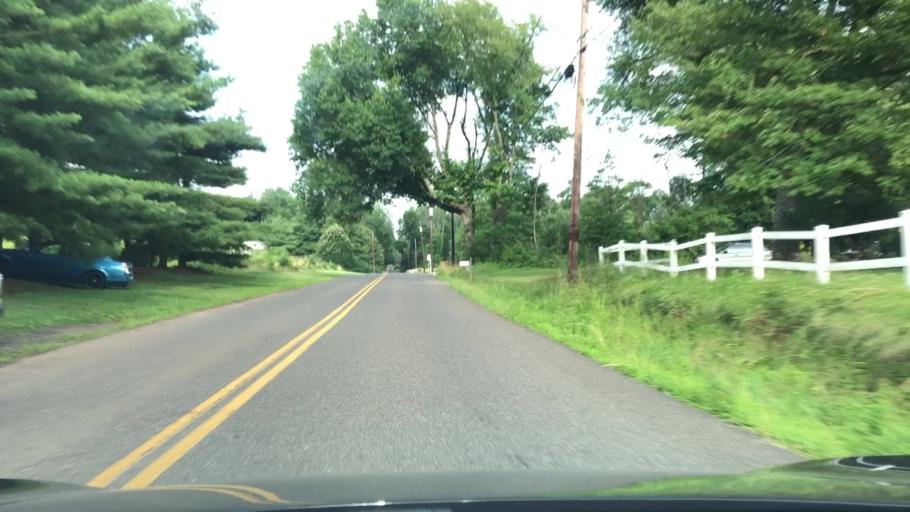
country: US
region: New Jersey
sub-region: Mercer County
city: Pennington
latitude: 40.3399
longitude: -74.7976
